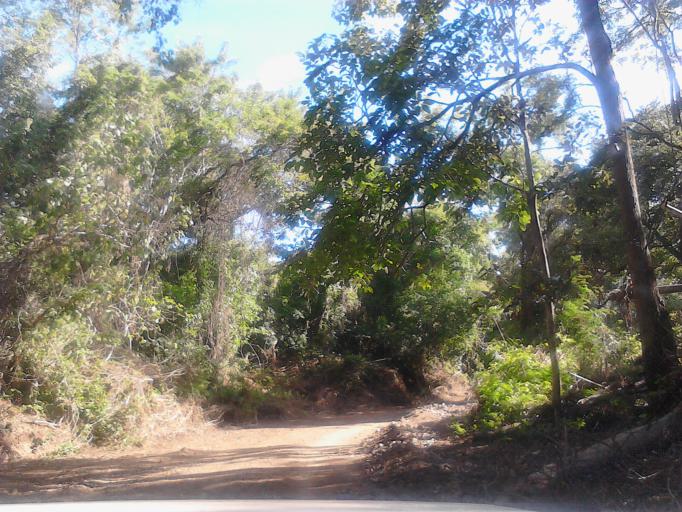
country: NI
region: Rivas
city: Tola
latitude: 11.4998
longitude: -86.0499
